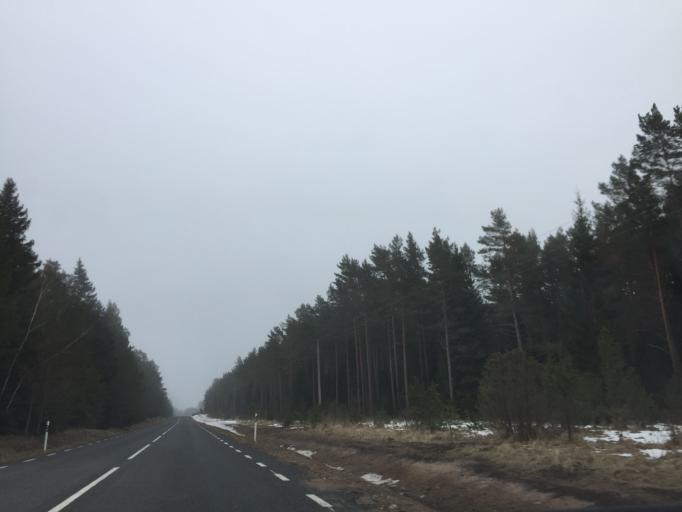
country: EE
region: Saare
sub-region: Kuressaare linn
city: Kuressaare
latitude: 58.4694
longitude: 22.0337
